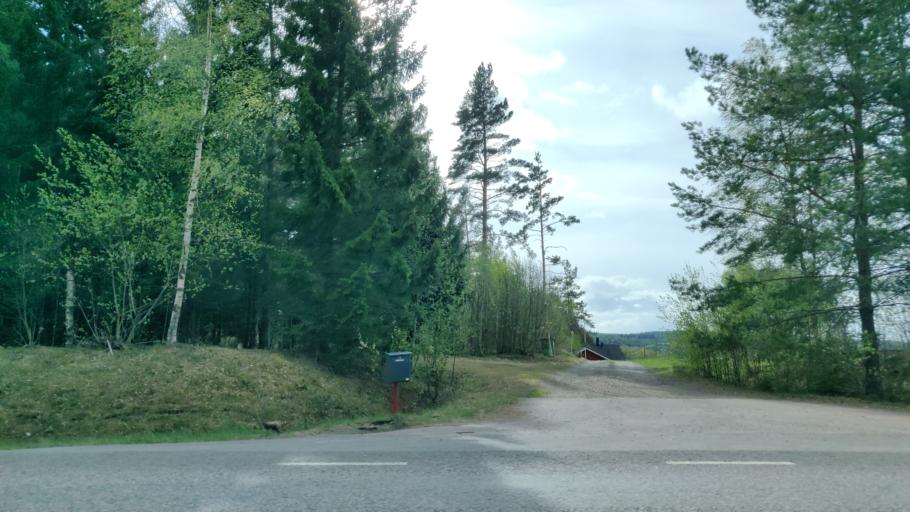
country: SE
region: Vaermland
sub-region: Forshaga Kommun
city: Deje
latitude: 59.5852
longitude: 13.4605
